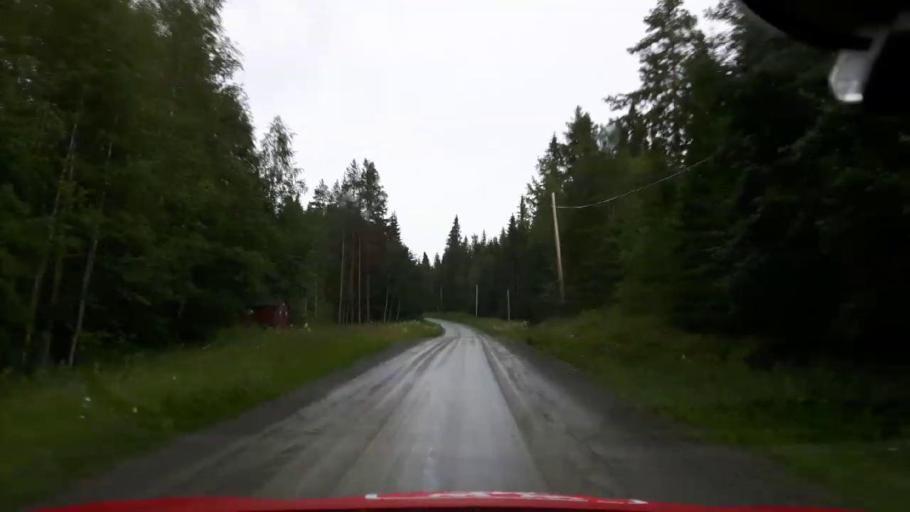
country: SE
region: Jaemtland
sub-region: OEstersunds Kommun
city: Brunflo
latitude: 62.9019
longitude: 14.8600
